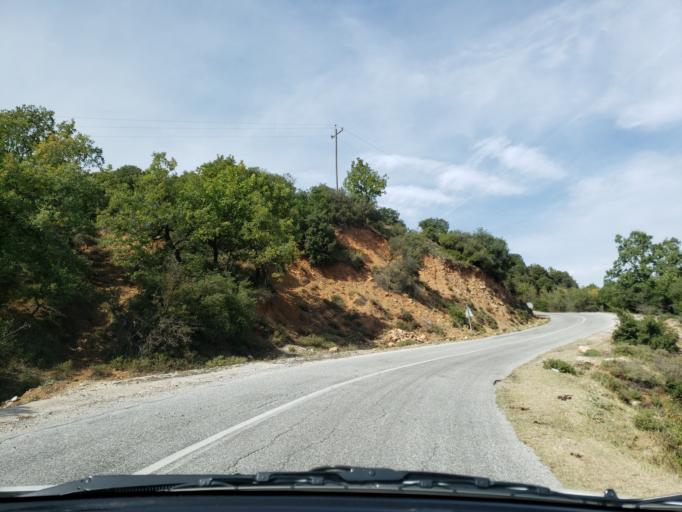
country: GR
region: Thessaly
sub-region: Trikala
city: Kalampaka
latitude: 39.7265
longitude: 21.6484
